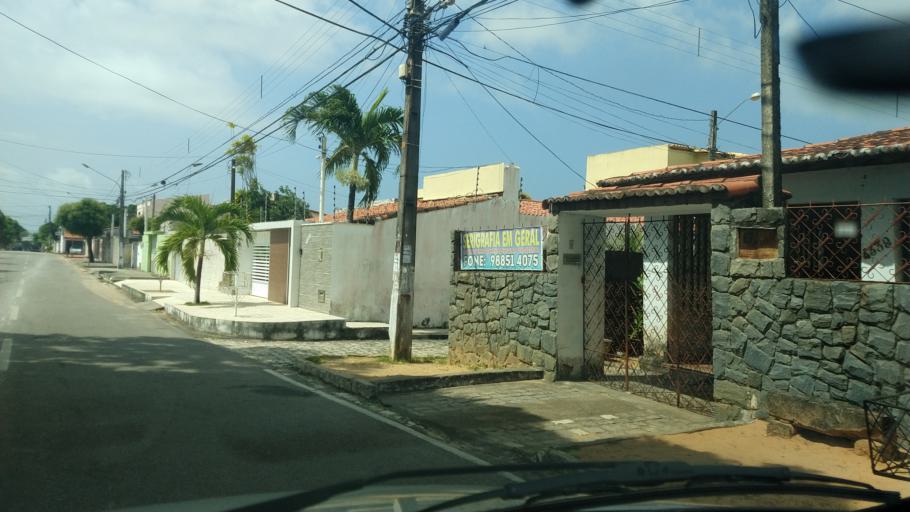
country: BR
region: Rio Grande do Norte
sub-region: Parnamirim
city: Parnamirim
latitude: -5.8681
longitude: -35.2107
